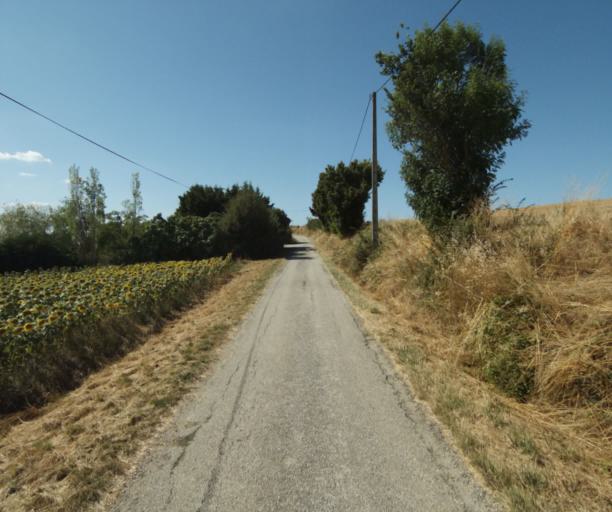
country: FR
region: Midi-Pyrenees
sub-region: Departement de la Haute-Garonne
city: Saint-Felix-Lauragais
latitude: 43.4787
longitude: 1.8991
